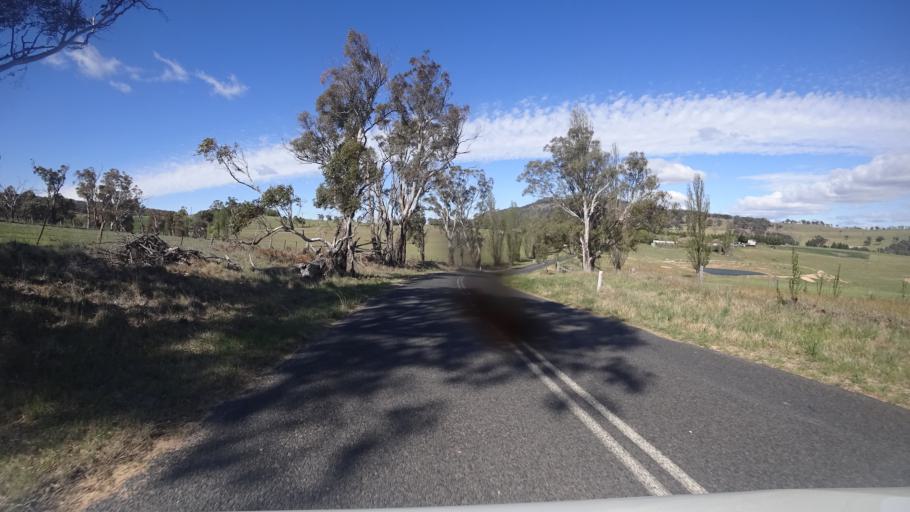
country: AU
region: New South Wales
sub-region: Lithgow
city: Portland
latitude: -33.5216
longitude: 149.9454
